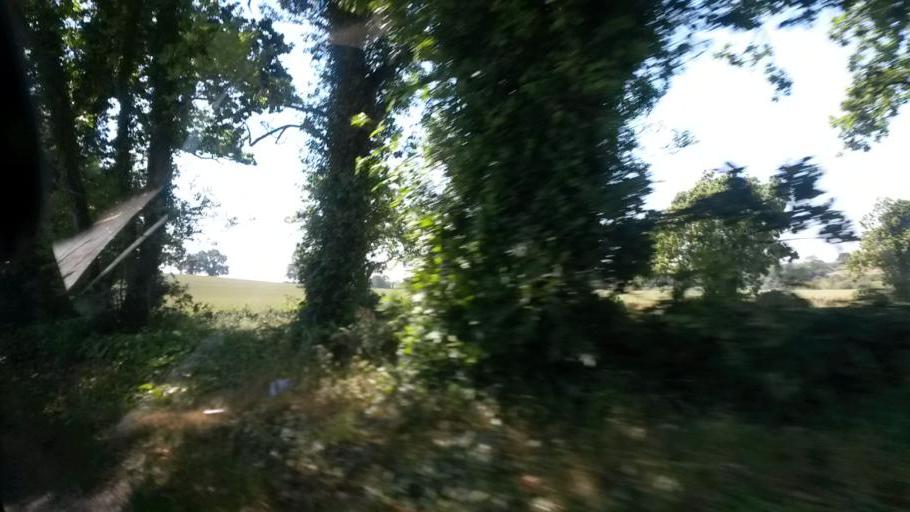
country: IE
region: Leinster
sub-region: An Mhi
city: Stamullin
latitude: 53.5843
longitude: -6.3010
